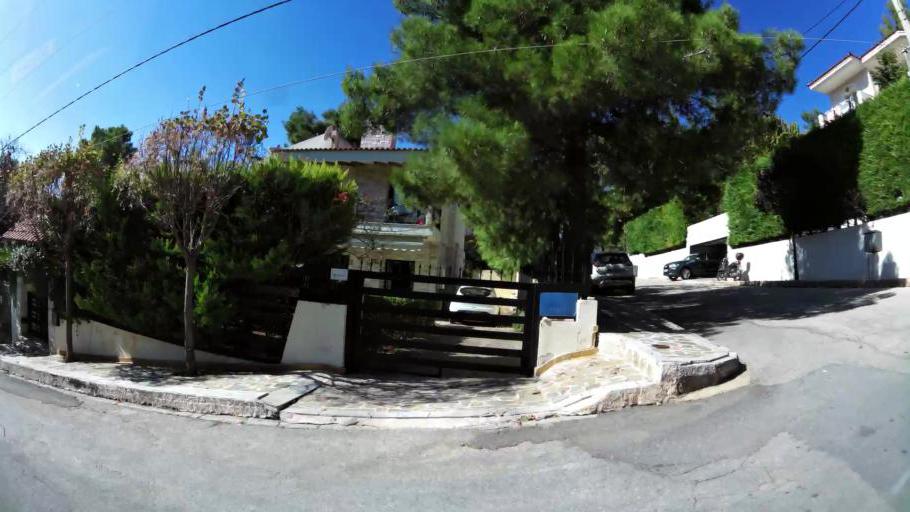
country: GR
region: Attica
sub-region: Nomarchia Anatolikis Attikis
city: Rodopoli
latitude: 38.1093
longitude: 23.8822
